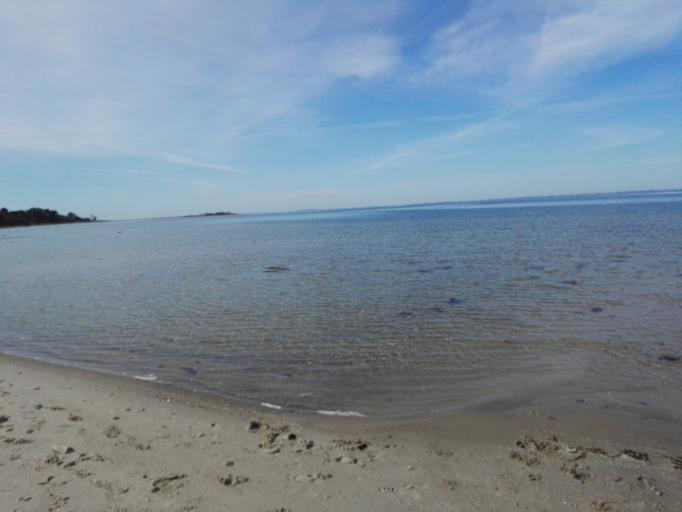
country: DK
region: Capital Region
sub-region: Halsnaes Kommune
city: Hundested
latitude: 55.9359
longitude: 11.9060
